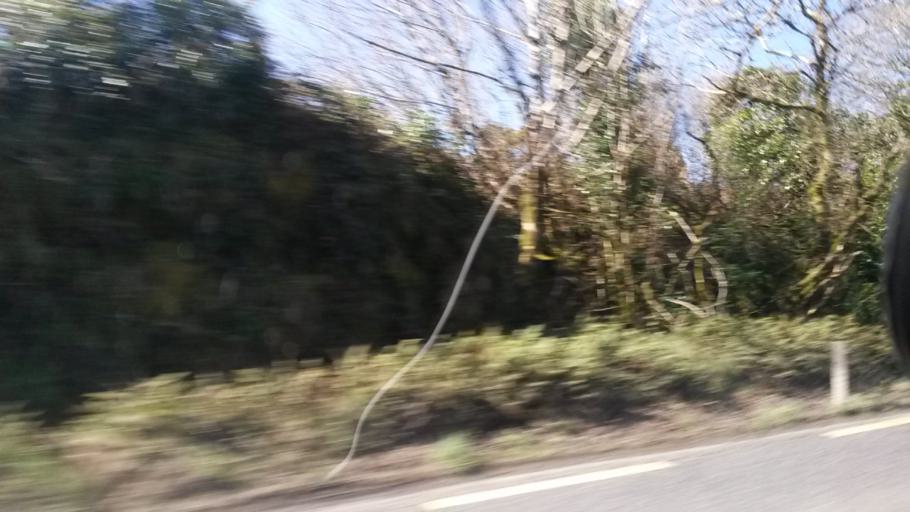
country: IE
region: Munster
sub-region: County Cork
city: Macroom
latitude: 51.9187
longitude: -9.0725
